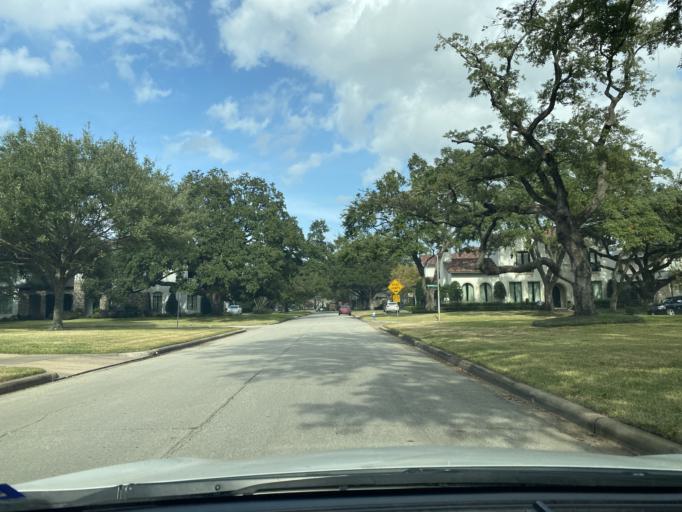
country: US
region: Texas
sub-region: Harris County
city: Hunters Creek Village
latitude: 29.7530
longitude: -95.4740
